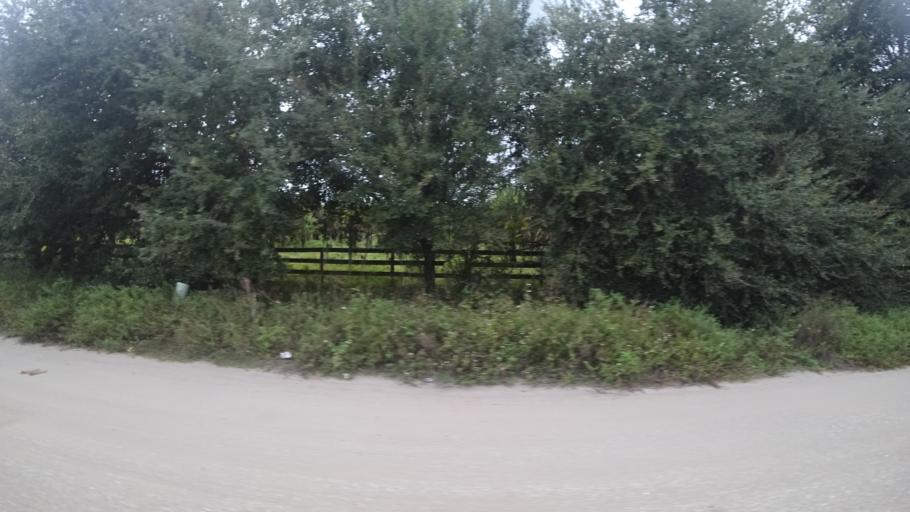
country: US
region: Florida
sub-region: Sarasota County
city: Lake Sarasota
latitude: 27.3860
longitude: -82.2503
